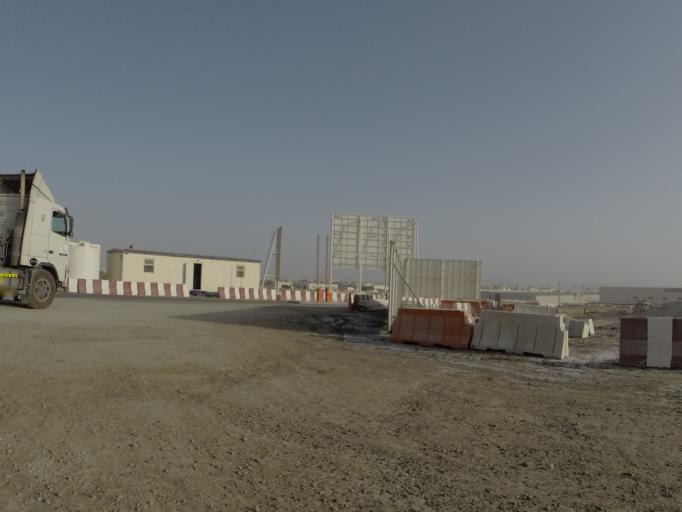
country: AE
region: Dubai
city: Dubai
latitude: 24.9682
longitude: 55.1629
